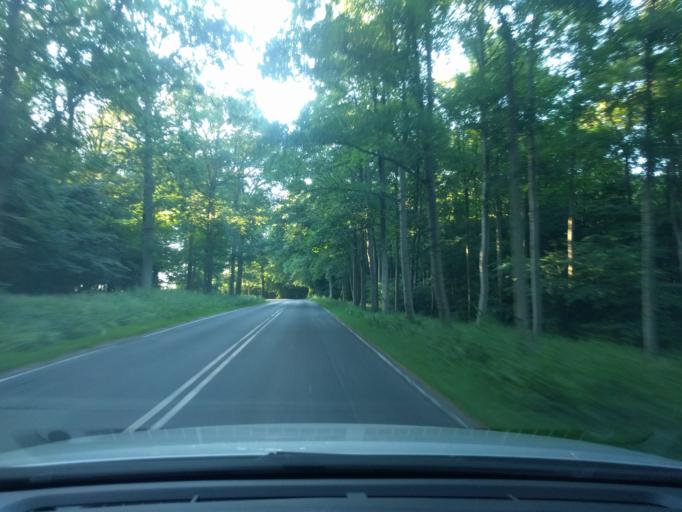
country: DK
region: South Denmark
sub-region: Kerteminde Kommune
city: Kerteminde
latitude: 55.5305
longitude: 10.6514
